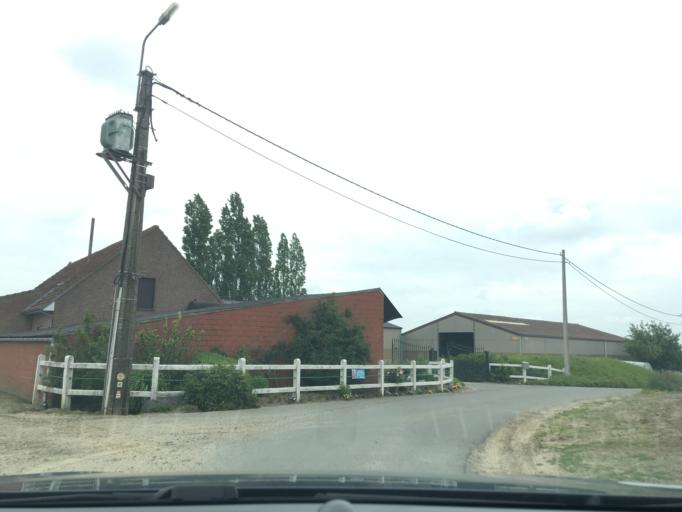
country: BE
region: Flanders
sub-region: Provincie West-Vlaanderen
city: Moorslede
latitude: 50.8925
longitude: 3.0866
